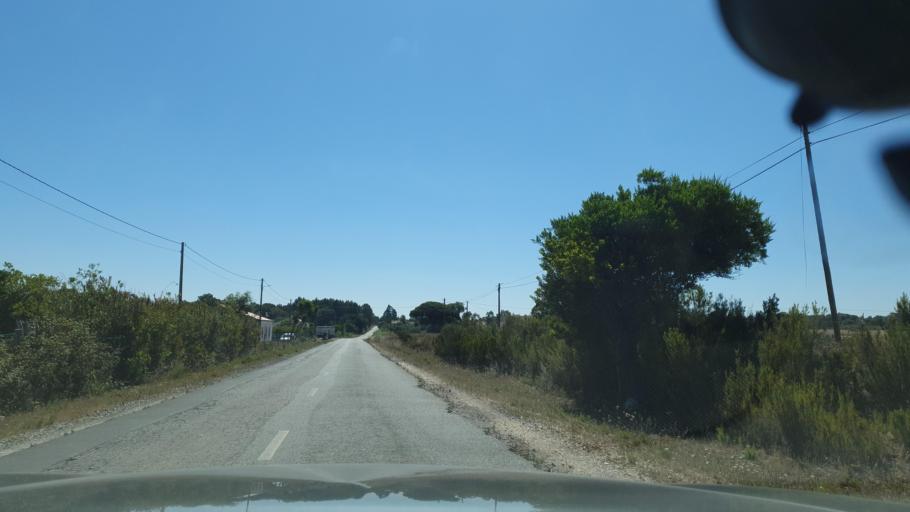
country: PT
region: Beja
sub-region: Odemira
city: Sao Teotonio
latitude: 37.4998
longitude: -8.6760
